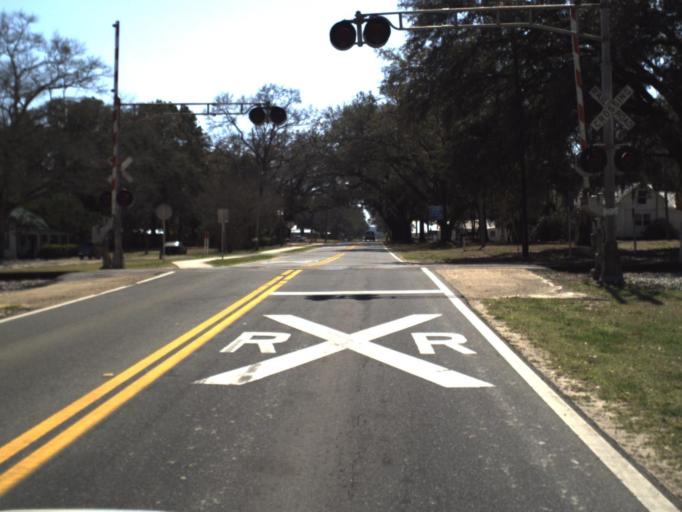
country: US
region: Florida
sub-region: Jackson County
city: Sneads
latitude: 30.7125
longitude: -85.0202
